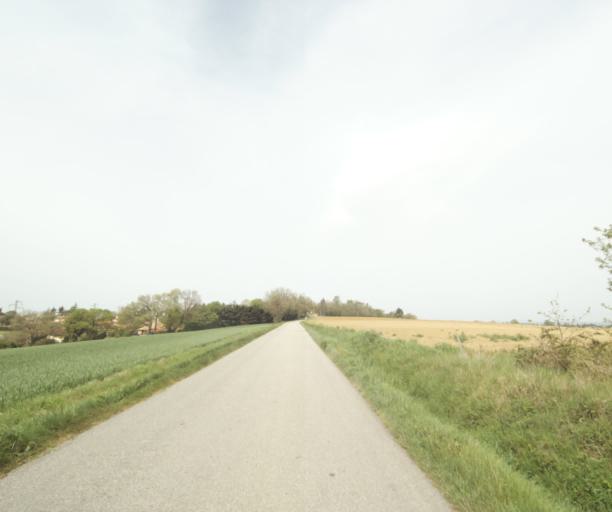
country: FR
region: Midi-Pyrenees
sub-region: Departement de la Haute-Garonne
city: Pompertuzat
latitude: 43.4869
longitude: 1.5010
